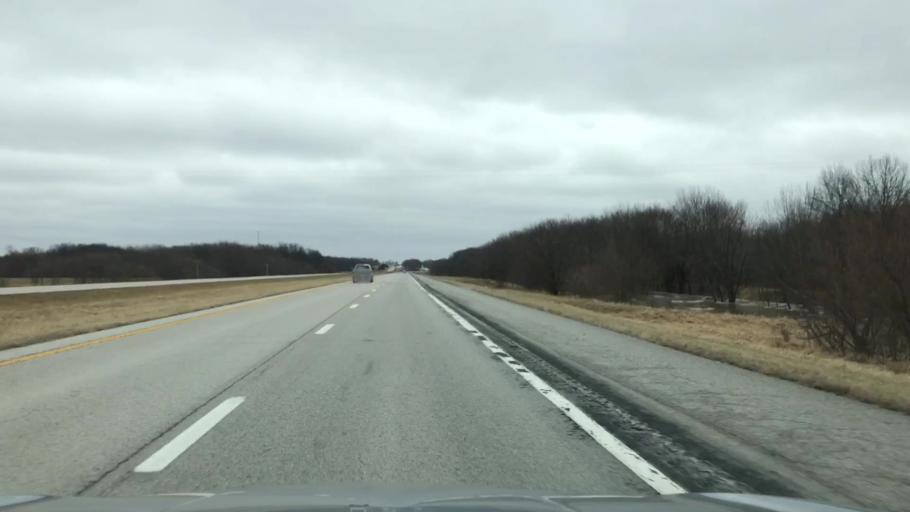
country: US
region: Missouri
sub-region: Linn County
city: Linneus
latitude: 39.7775
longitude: -93.3304
